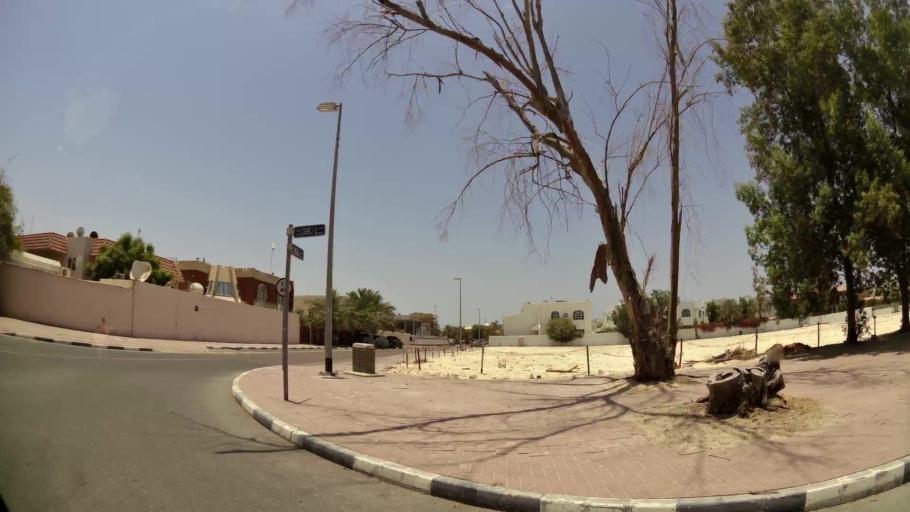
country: AE
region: Dubai
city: Dubai
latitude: 25.2162
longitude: 55.2578
